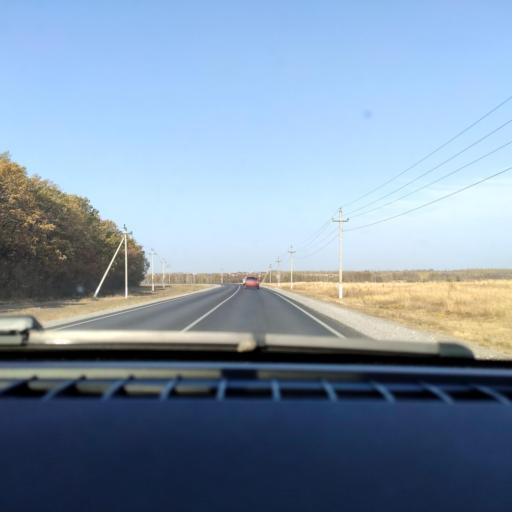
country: RU
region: Voronezj
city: Novaya Usman'
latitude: 51.6903
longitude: 39.3948
